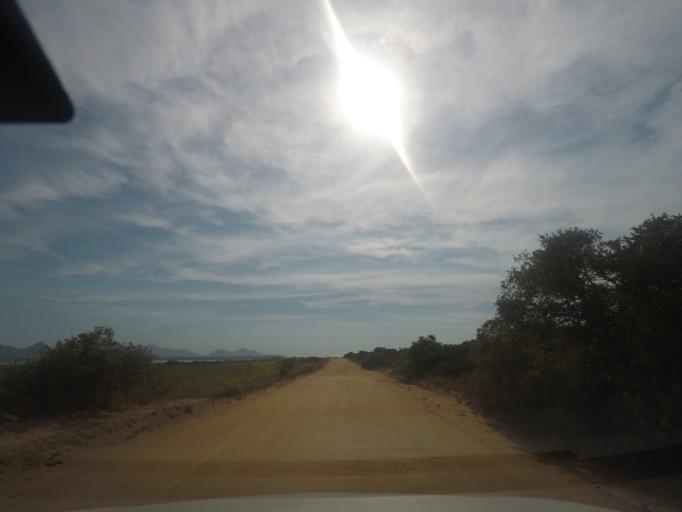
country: BR
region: Rio de Janeiro
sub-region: Marica
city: Marica
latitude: -22.9597
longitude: -42.8719
